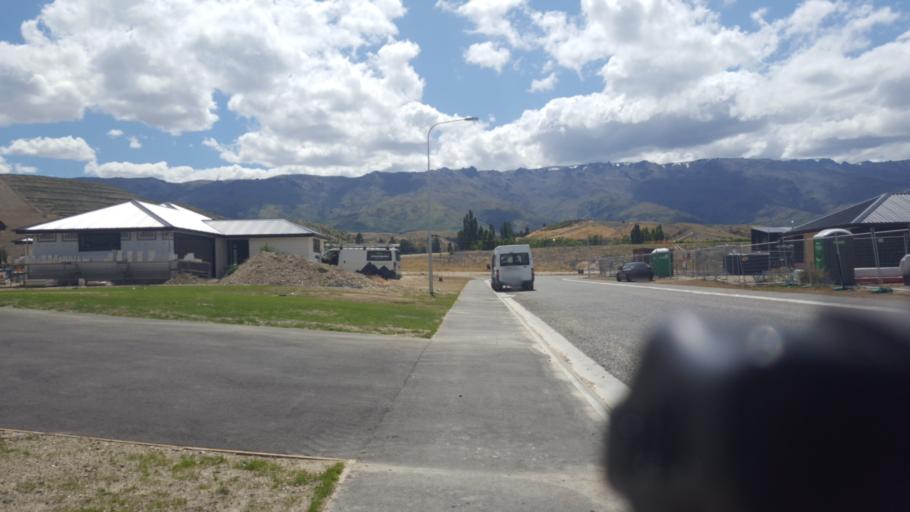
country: NZ
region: Otago
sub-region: Queenstown-Lakes District
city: Wanaka
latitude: -44.9765
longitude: 169.2392
